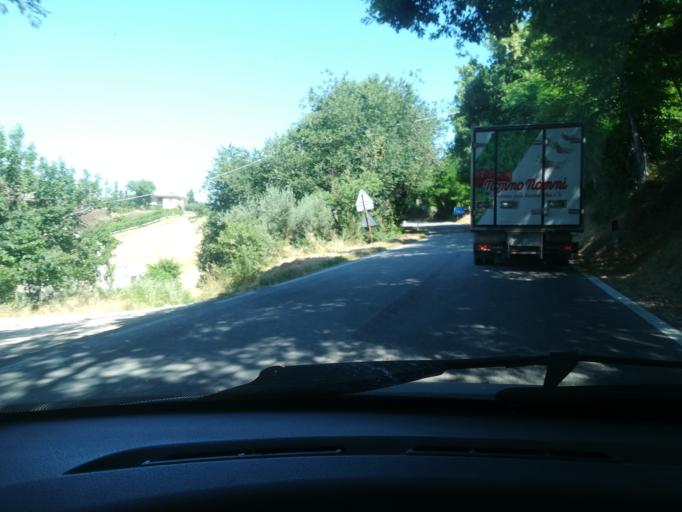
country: IT
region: The Marches
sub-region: Provincia di Macerata
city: San Ginesio
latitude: 43.1119
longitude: 13.3466
